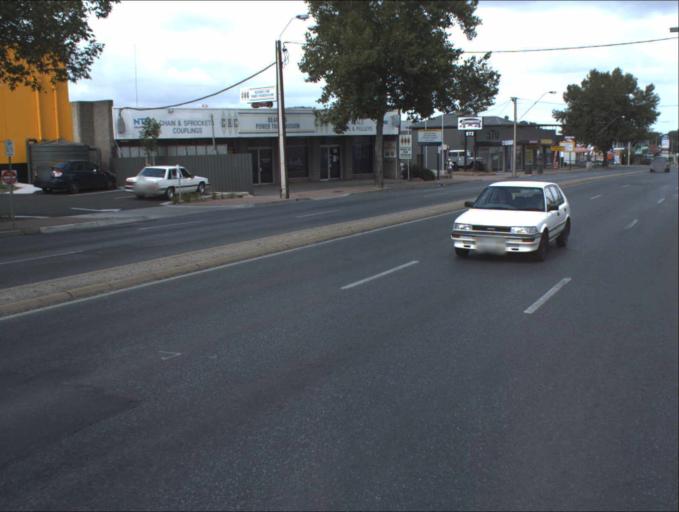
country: AU
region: South Australia
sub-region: Port Adelaide Enfield
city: Gilles Plains
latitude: -34.8549
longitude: 138.6604
